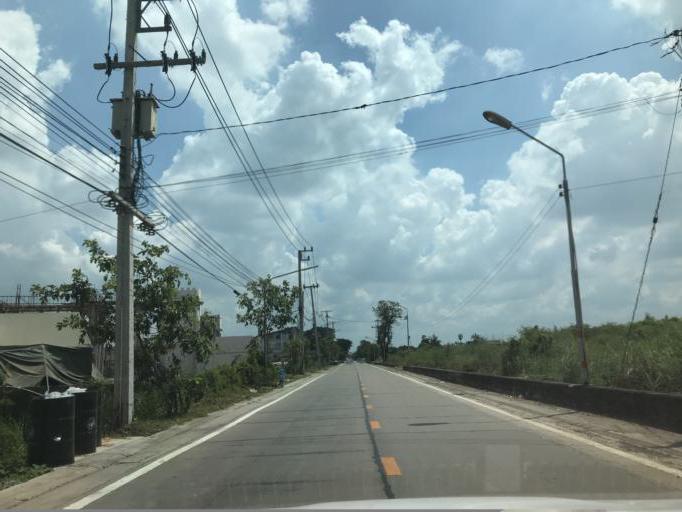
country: TH
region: Pathum Thani
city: Pathum Thani
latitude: 14.0129
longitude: 100.5398
